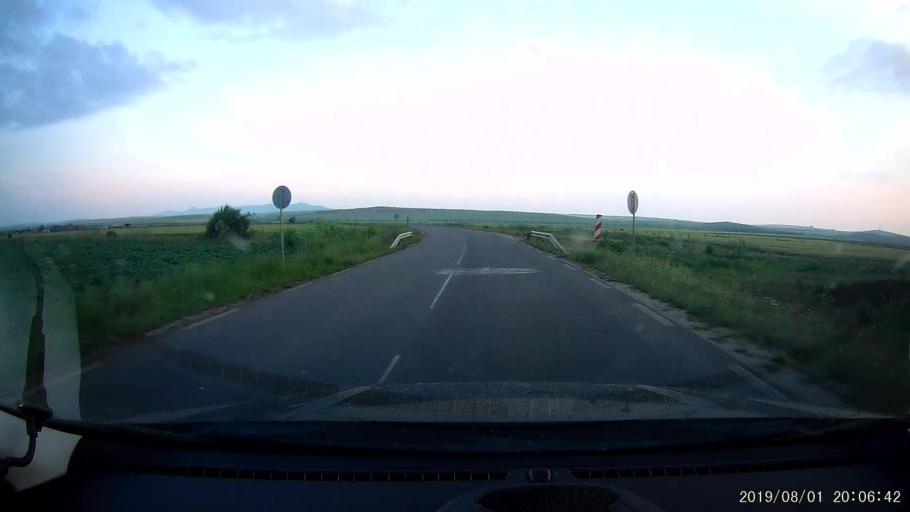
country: BG
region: Yambol
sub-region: Obshtina Yambol
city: Yambol
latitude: 42.5318
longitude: 26.5574
